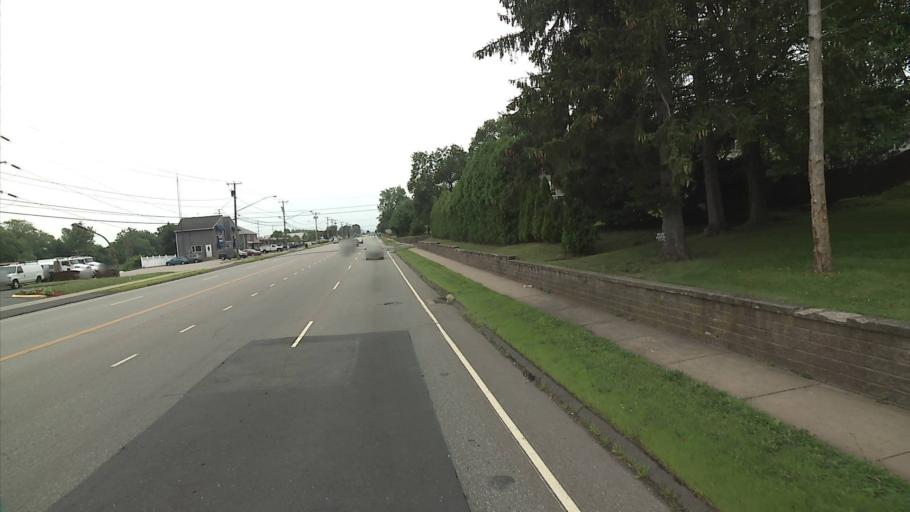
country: US
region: Connecticut
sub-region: Hartford County
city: Wethersfield
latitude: 41.7033
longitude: -72.6605
